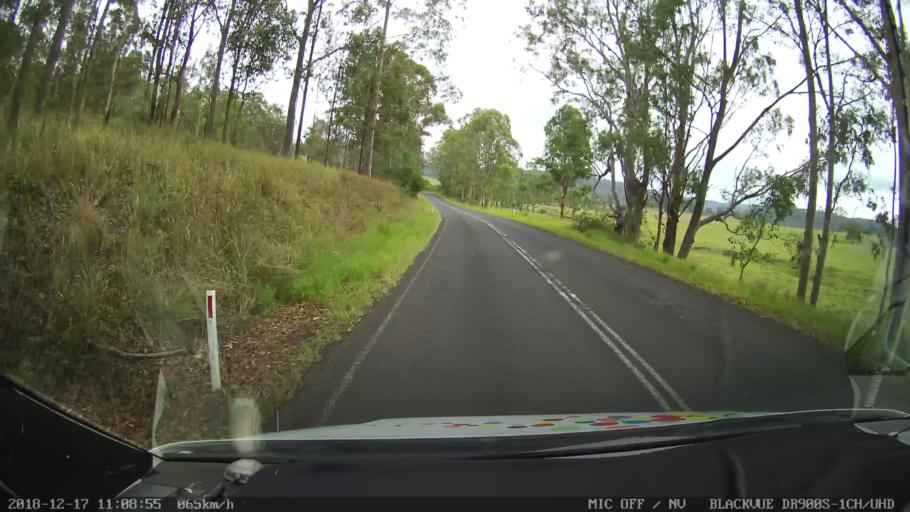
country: AU
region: New South Wales
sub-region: Kyogle
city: Kyogle
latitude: -28.7590
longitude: 152.6555
